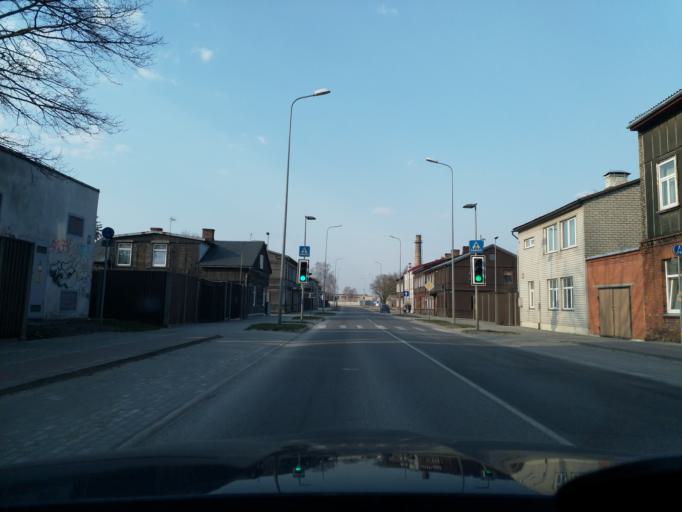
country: LV
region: Liepaja
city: Liepaja
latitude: 56.5075
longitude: 21.0253
